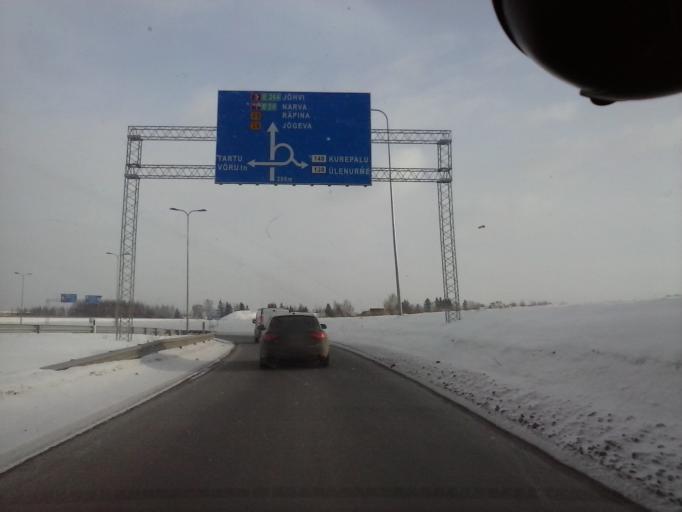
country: EE
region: Tartu
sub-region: UElenurme vald
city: Ulenurme
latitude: 58.3442
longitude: 26.7071
